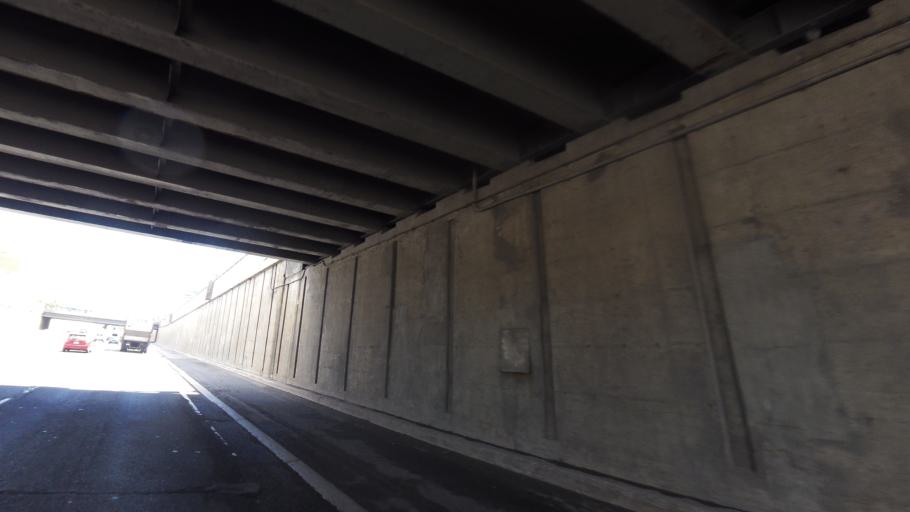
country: CA
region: Quebec
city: Hampstead
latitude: 45.4860
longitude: -73.6346
